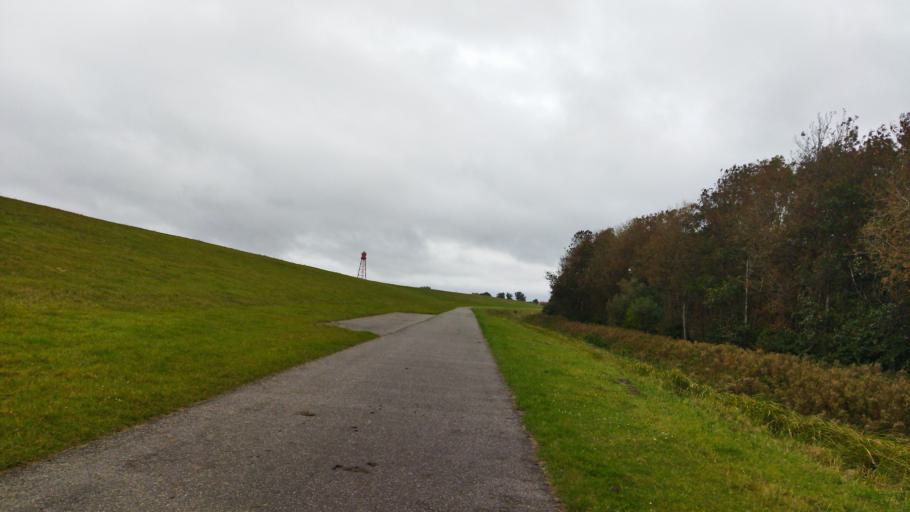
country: NL
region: Groningen
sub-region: Gemeente Delfzijl
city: Delfzijl
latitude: 53.3972
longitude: 7.0137
